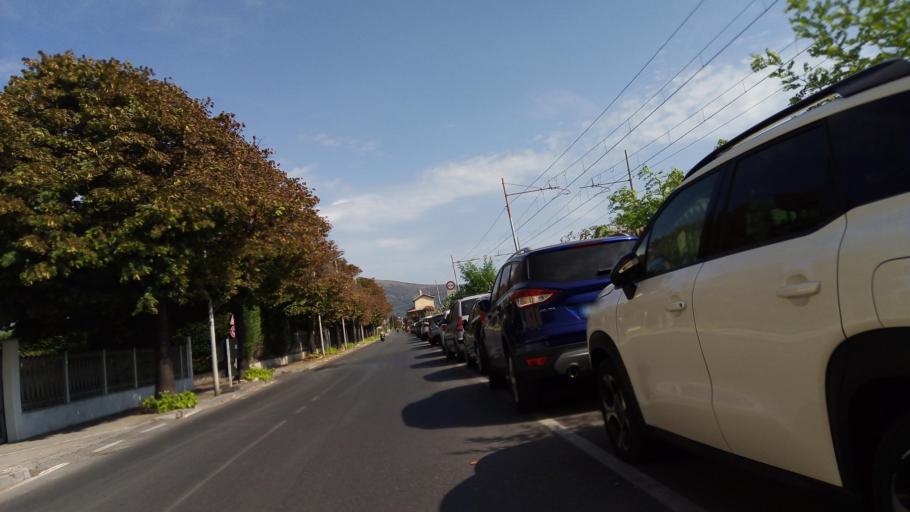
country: IT
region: Liguria
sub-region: Provincia di Savona
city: Albenga
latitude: 44.0595
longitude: 8.2250
